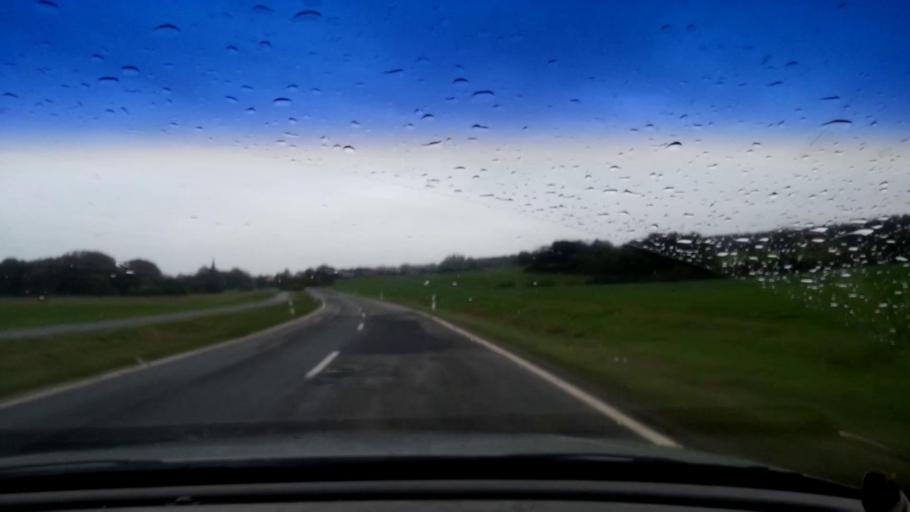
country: DE
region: Bavaria
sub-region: Upper Franconia
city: Burgebrach
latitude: 49.8468
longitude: 10.7203
